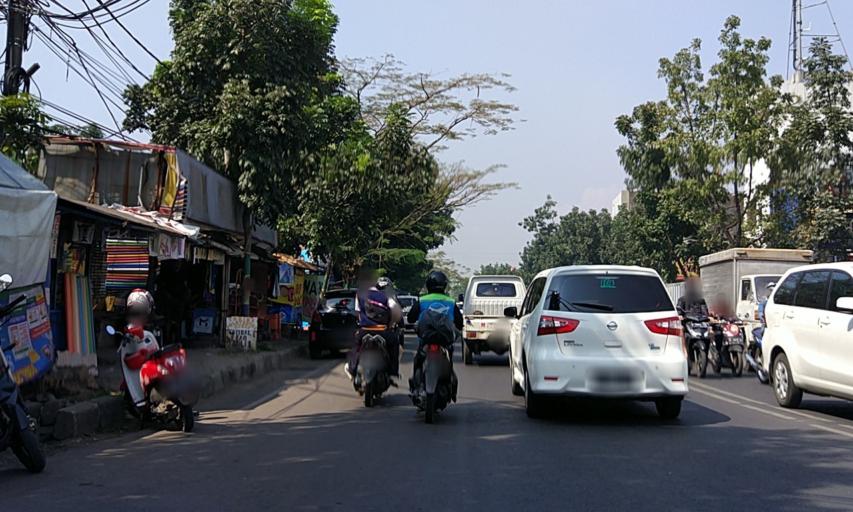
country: ID
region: West Java
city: Bandung
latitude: -6.9392
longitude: 107.6063
